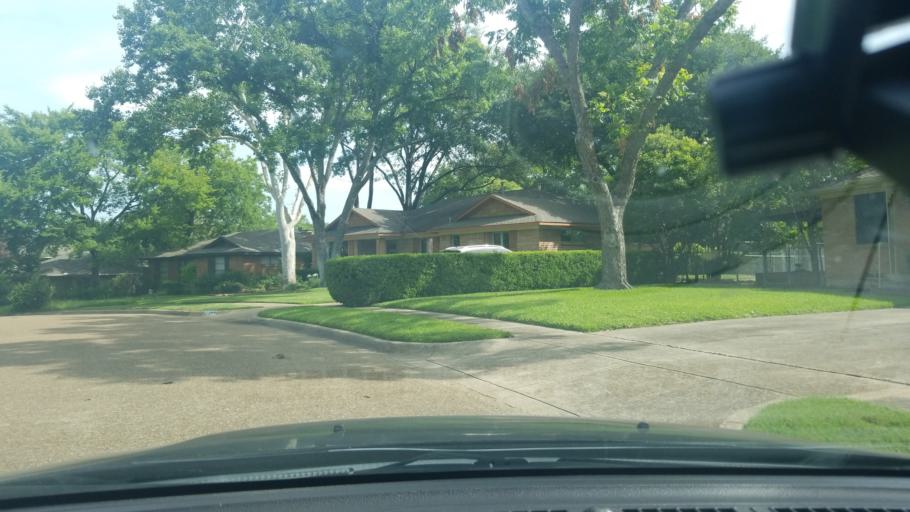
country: US
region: Texas
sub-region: Dallas County
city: Highland Park
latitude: 32.8061
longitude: -96.7046
